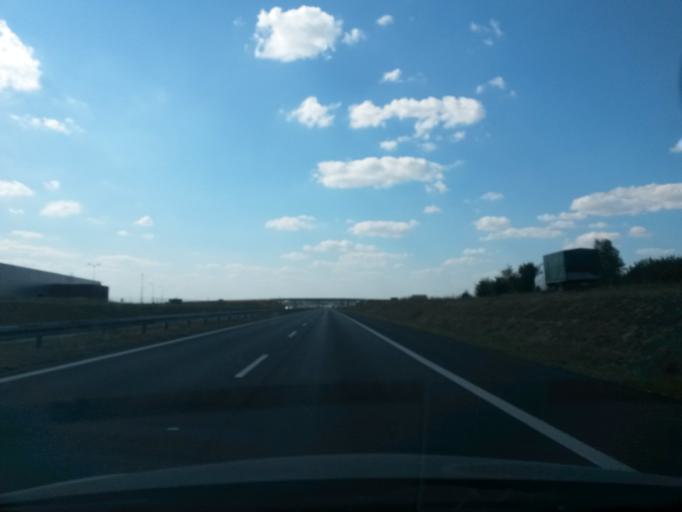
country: PL
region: Masovian Voivodeship
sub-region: Powiat nowodworski
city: Zakroczym
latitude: 52.4440
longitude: 20.6193
